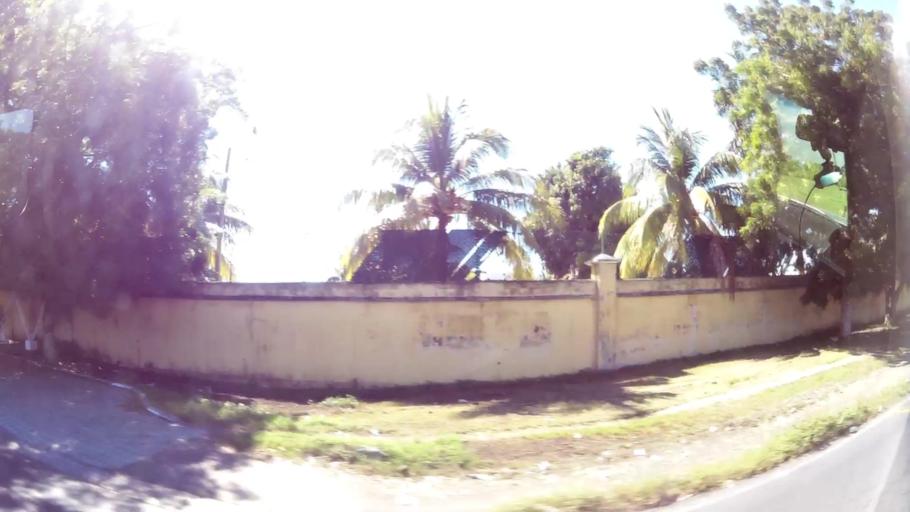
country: GT
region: Escuintla
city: Iztapa
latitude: 13.9402
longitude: -90.7152
